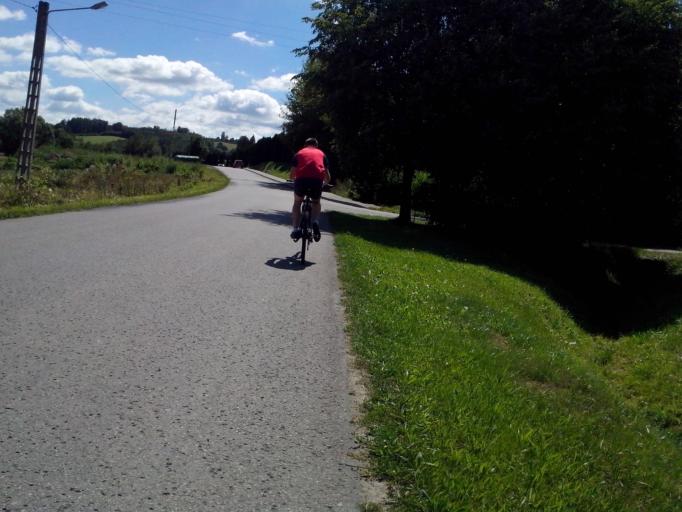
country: PL
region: Subcarpathian Voivodeship
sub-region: Powiat brzozowski
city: Golcowa
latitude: 49.7764
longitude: 21.9992
